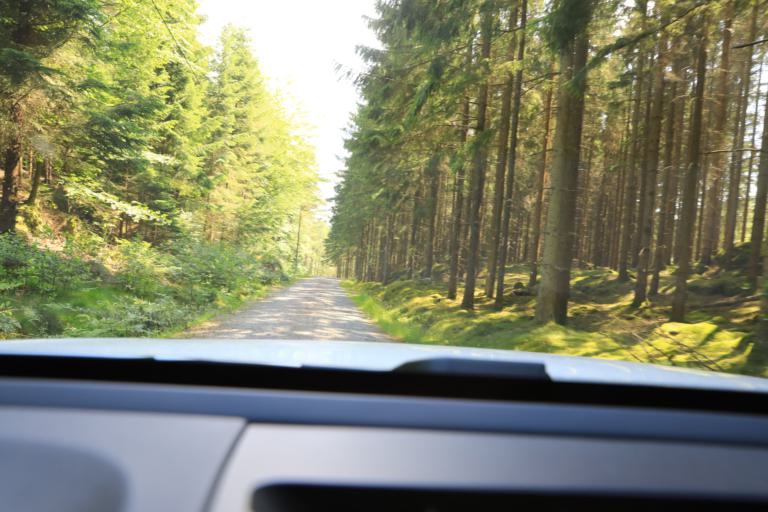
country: SE
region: Halland
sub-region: Varbergs Kommun
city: Veddige
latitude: 57.2143
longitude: 12.3482
